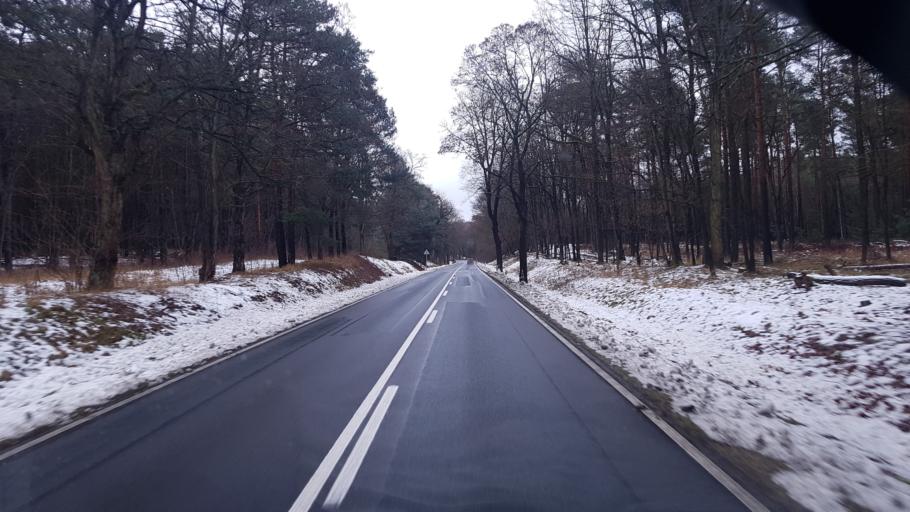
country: DE
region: Brandenburg
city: Jamlitz
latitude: 51.9882
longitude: 14.3853
